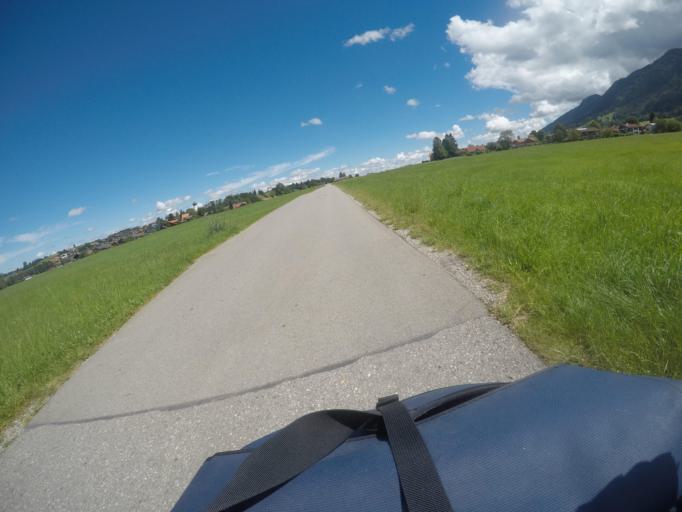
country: DE
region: Bavaria
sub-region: Swabia
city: Halblech
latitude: 47.6201
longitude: 10.8009
